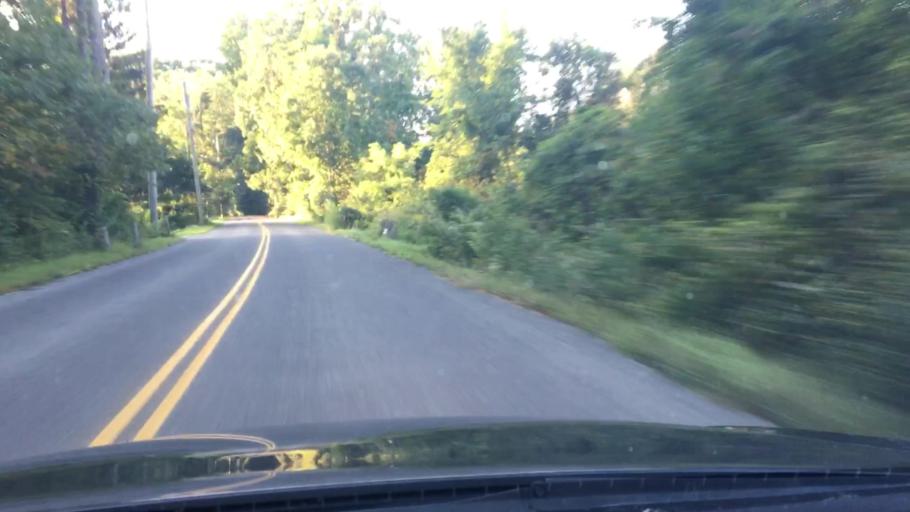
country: US
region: Connecticut
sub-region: Litchfield County
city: New Milford
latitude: 41.6179
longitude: -73.3735
